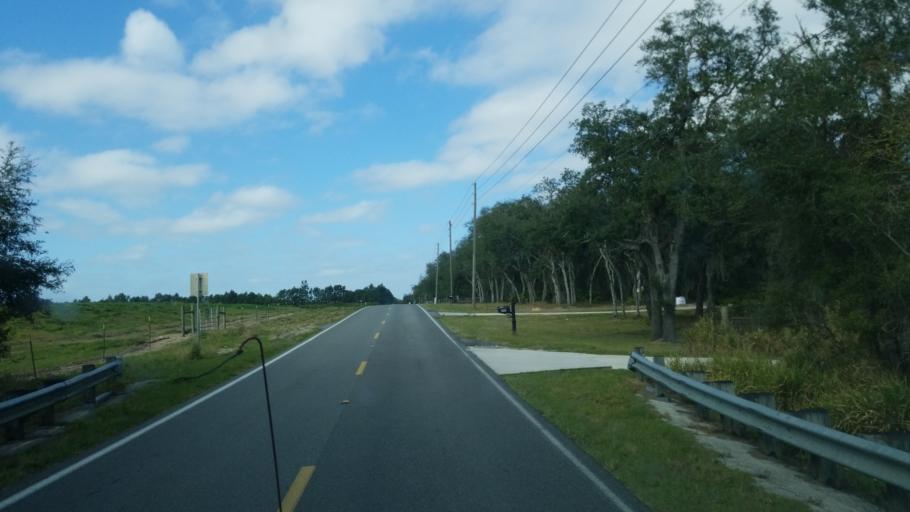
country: US
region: Florida
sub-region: Polk County
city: Lake Wales
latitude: 27.9251
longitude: -81.5146
